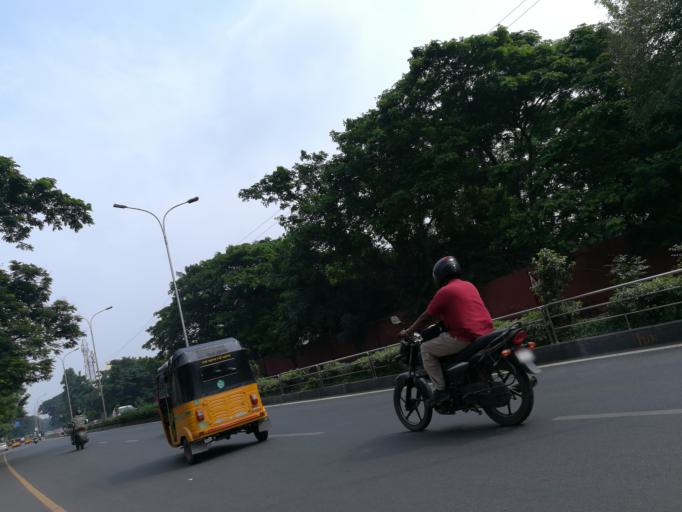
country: IN
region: Tamil Nadu
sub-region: Chennai
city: Gandhi Nagar
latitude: 13.0161
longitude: 80.2406
